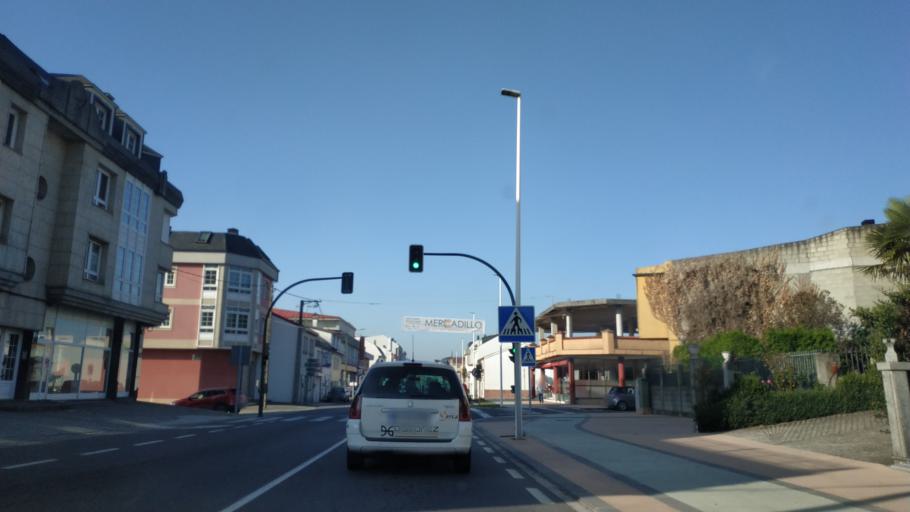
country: ES
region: Galicia
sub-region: Provincia da Coruna
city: Carballo
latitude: 43.2235
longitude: -8.6821
